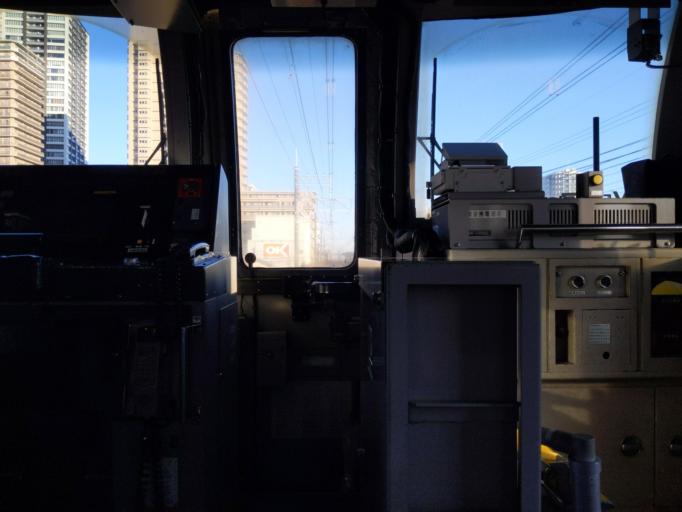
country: JP
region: Tokyo
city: Urayasu
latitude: 35.7226
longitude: 139.9235
